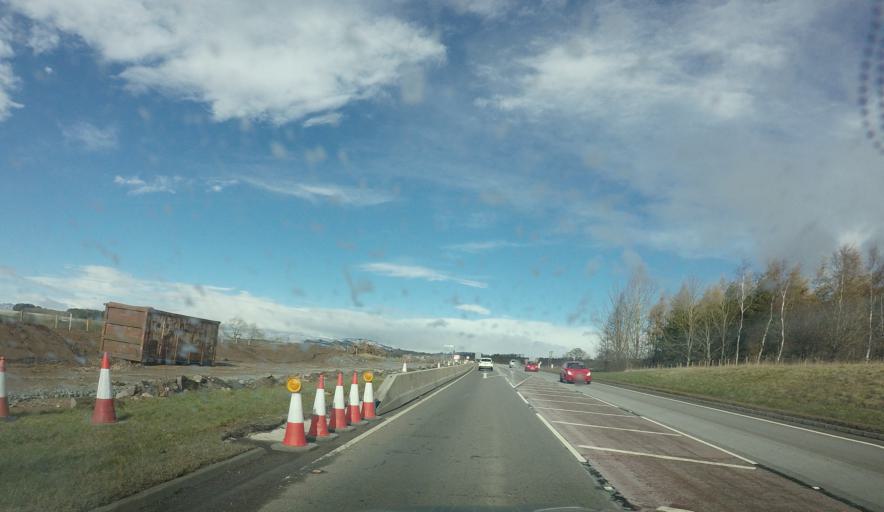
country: GB
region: Scotland
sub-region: Perth and Kinross
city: Luncarty
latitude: 56.4660
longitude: -3.4795
